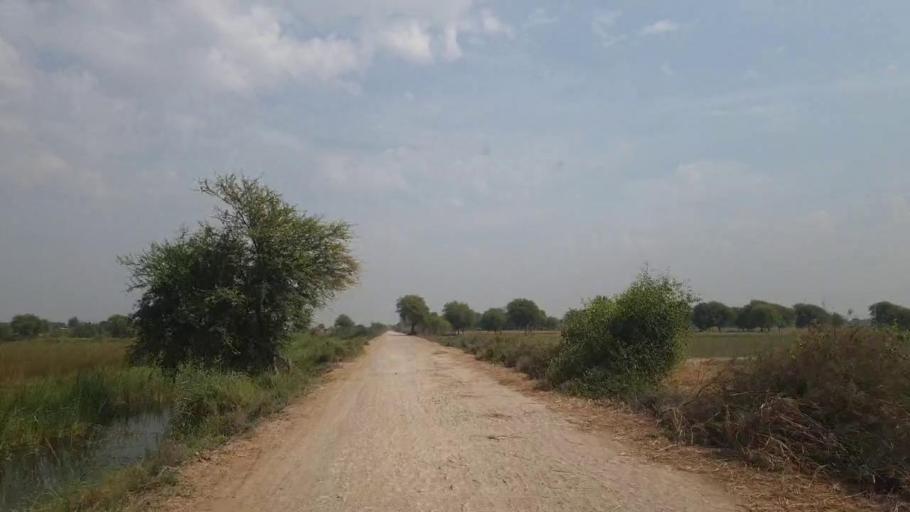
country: PK
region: Sindh
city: Rajo Khanani
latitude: 24.9555
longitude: 68.9863
